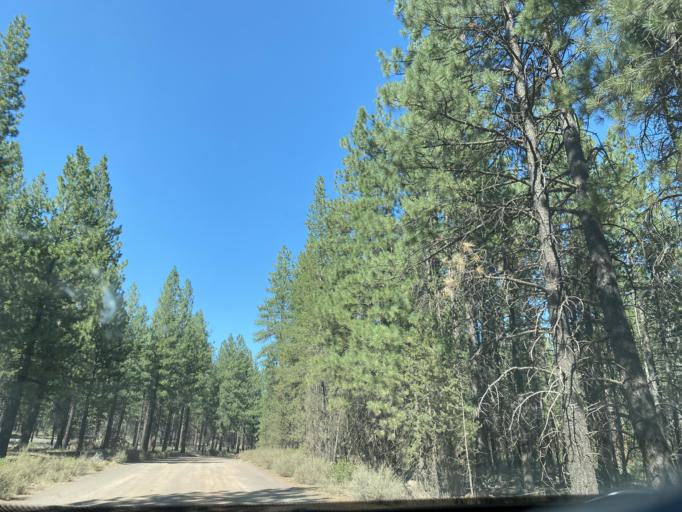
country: US
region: Oregon
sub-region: Deschutes County
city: Sunriver
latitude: 43.8686
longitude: -121.4838
